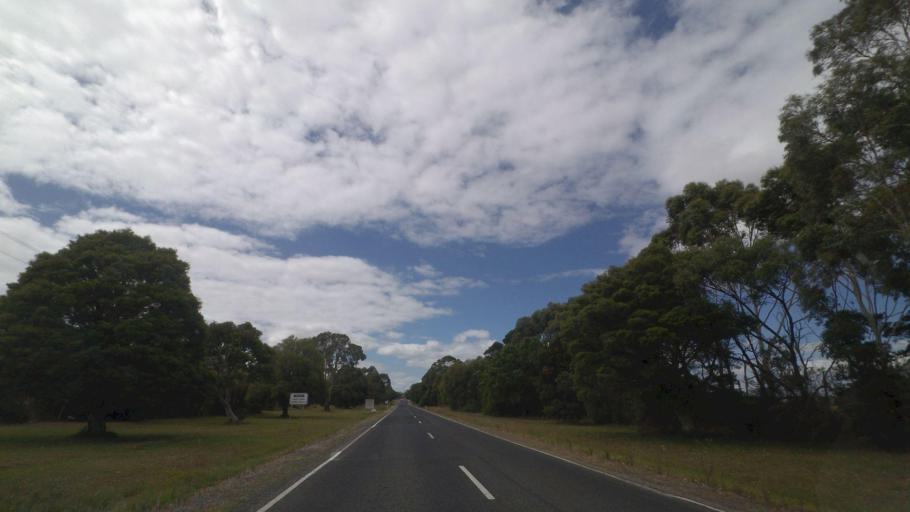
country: AU
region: Victoria
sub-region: Cardinia
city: Koo-Wee-Rup
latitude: -38.2629
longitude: 145.5584
